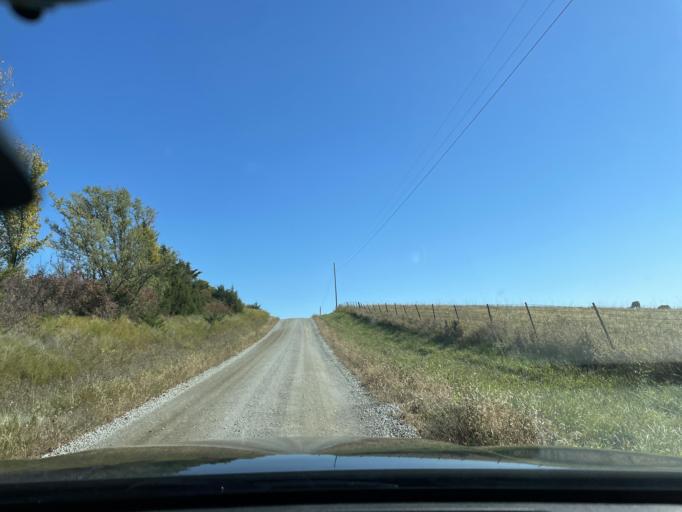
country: US
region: Missouri
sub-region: Andrew County
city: Savannah
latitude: 39.9396
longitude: -94.8738
